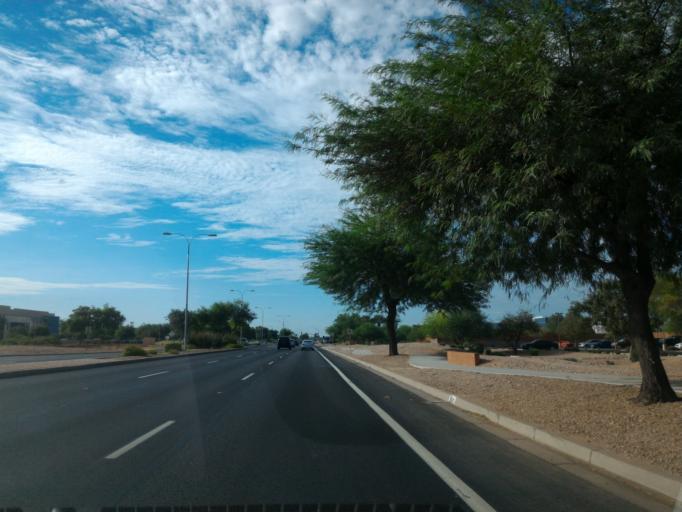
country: US
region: Arizona
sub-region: Maricopa County
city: Chandler
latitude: 33.2795
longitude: -111.8895
